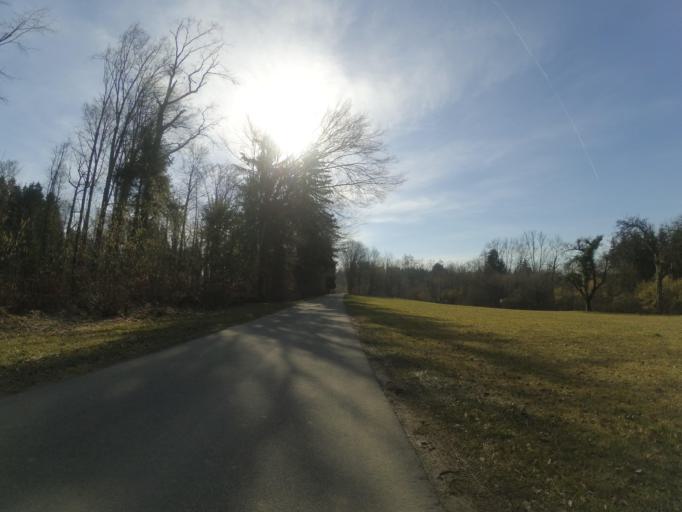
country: DE
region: Baden-Wuerttemberg
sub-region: Tuebingen Region
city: Meckenbeuren
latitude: 47.7176
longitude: 9.5678
